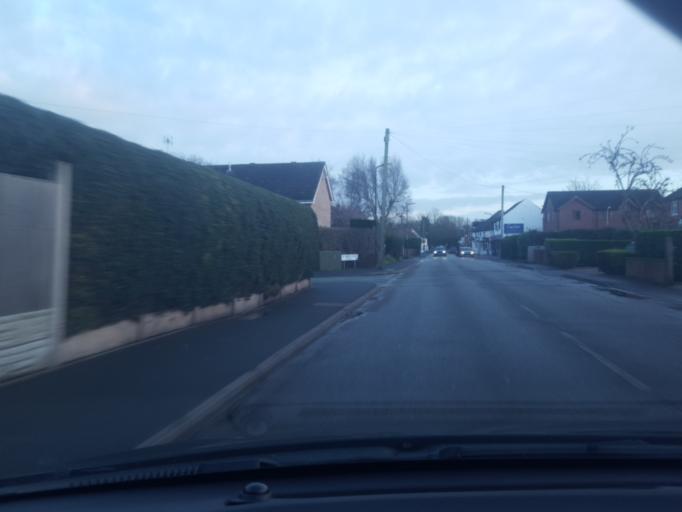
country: GB
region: England
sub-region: Shropshire
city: Albrighton
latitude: 52.6366
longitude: -2.2828
